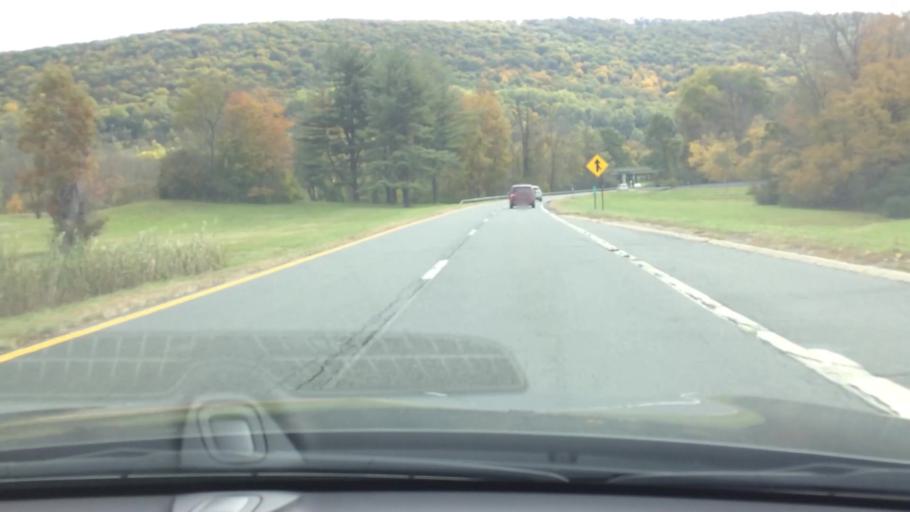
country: US
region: New York
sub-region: Dutchess County
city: Hillside Lake
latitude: 41.5415
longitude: -73.7731
